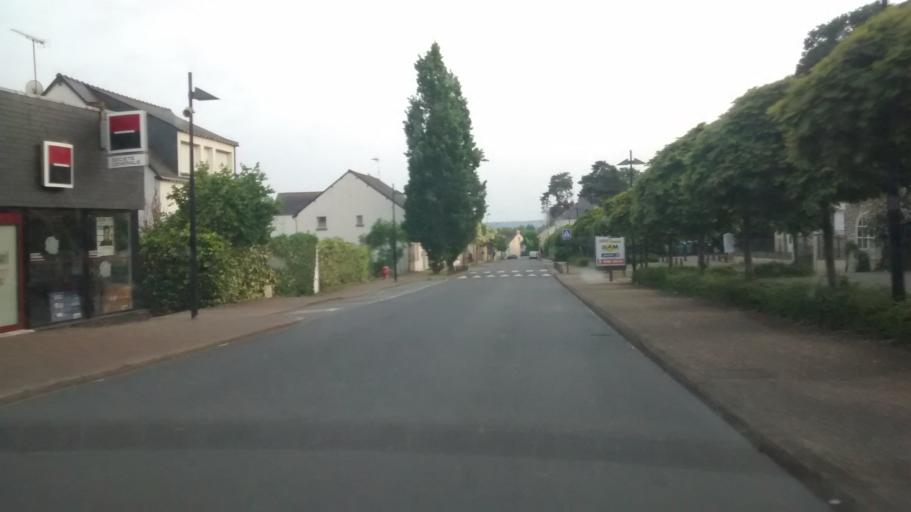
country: FR
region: Brittany
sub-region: Departement du Morbihan
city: Guer
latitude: 47.9423
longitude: -2.1319
